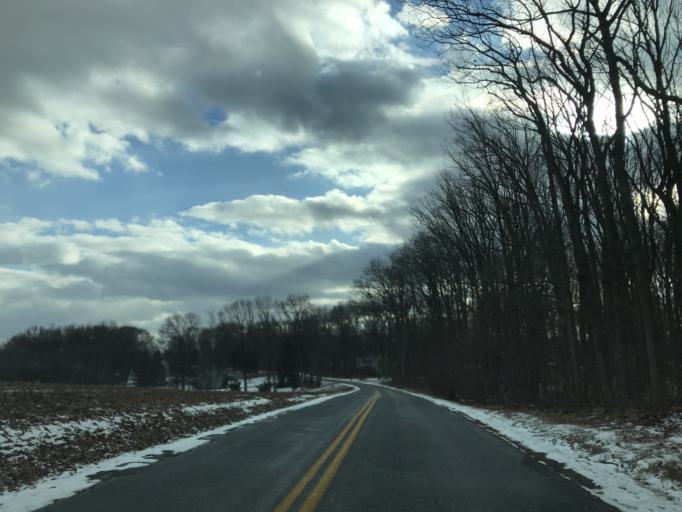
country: US
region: Maryland
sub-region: Harford County
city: Jarrettsville
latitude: 39.6371
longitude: -76.4881
